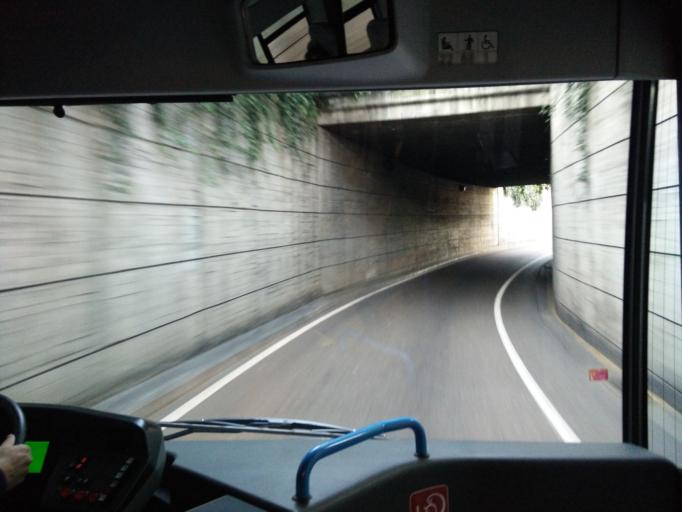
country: ES
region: Madrid
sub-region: Provincia de Madrid
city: Barajas de Madrid
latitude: 40.4664
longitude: -3.5706
